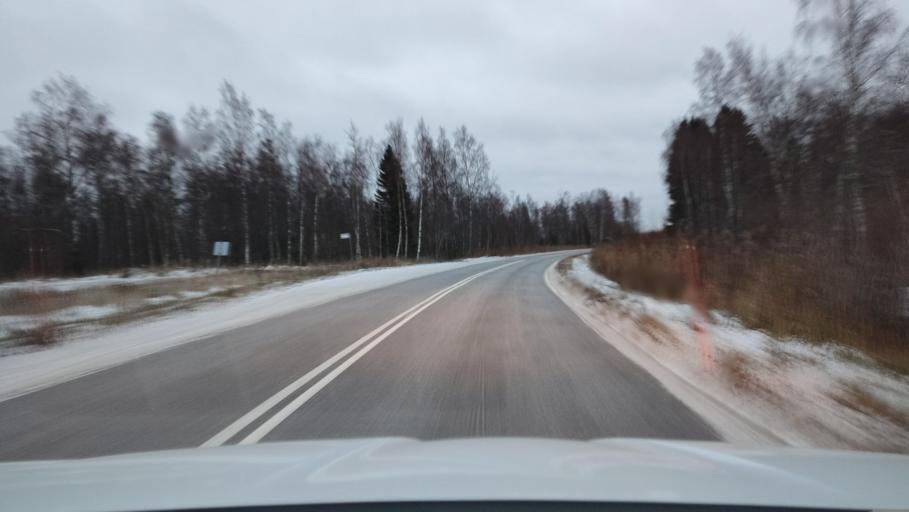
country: FI
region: Ostrobothnia
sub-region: Vaasa
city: Replot
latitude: 63.2810
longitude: 21.3395
